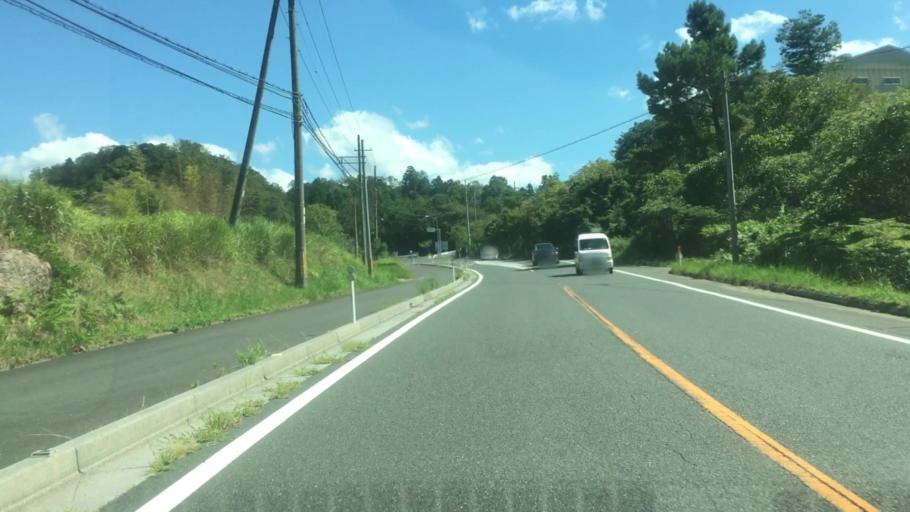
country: JP
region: Hyogo
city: Toyooka
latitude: 35.5851
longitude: 134.9531
